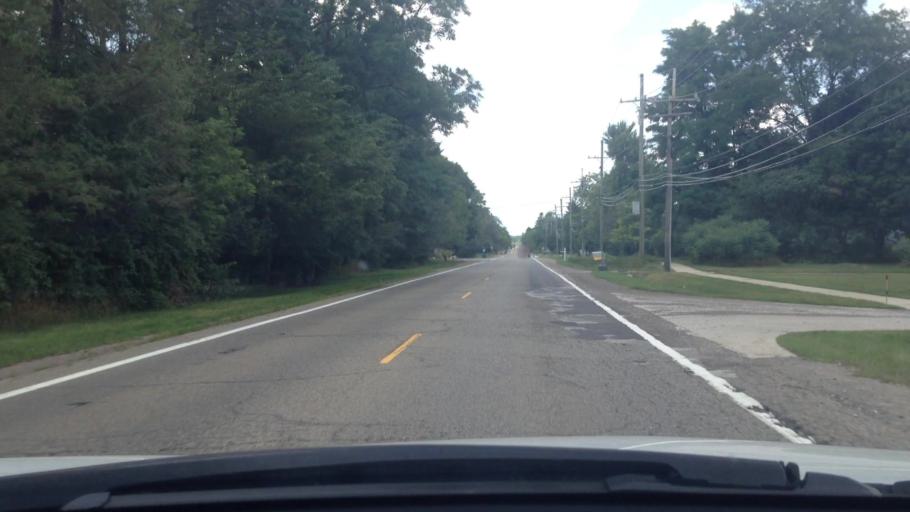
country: US
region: Michigan
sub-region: Oakland County
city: Waterford
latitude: 42.7099
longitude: -83.3489
